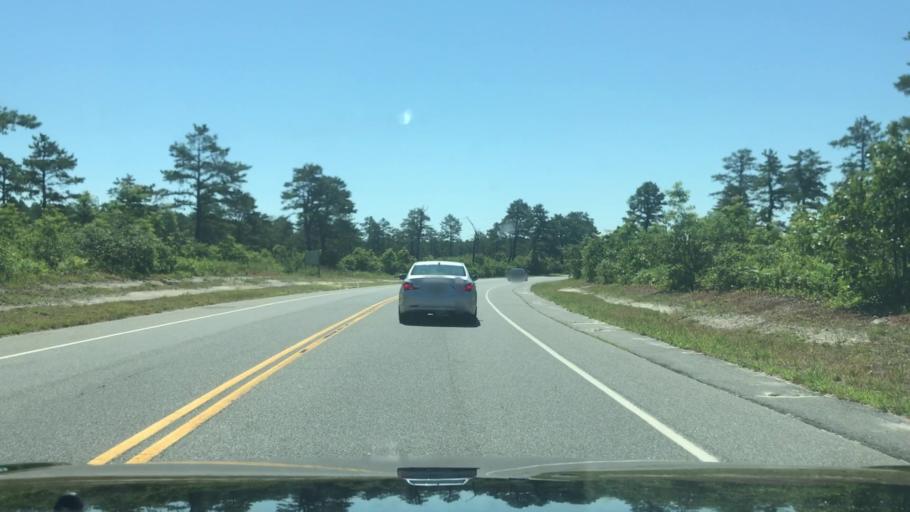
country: US
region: New Jersey
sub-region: Ocean County
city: Holiday City South
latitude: 39.9395
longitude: -74.2342
